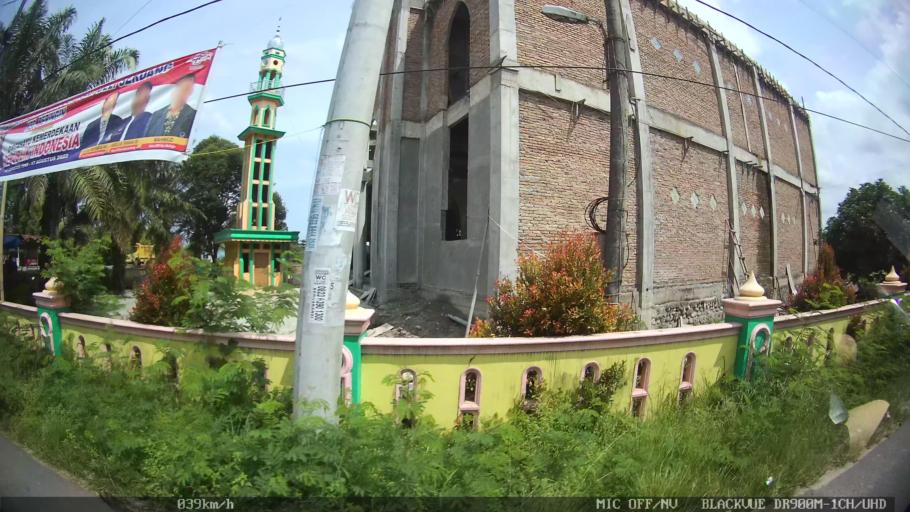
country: ID
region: North Sumatra
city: Percut
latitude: 3.6115
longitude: 98.8466
